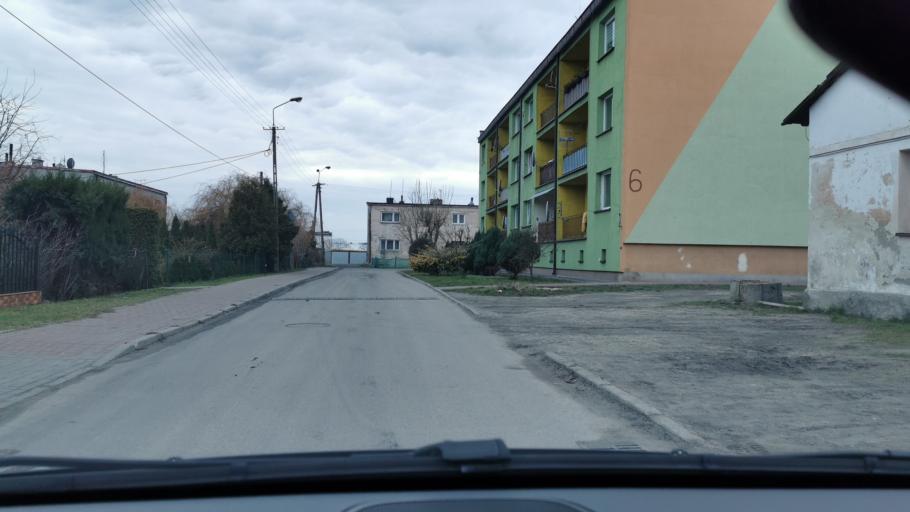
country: PL
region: Masovian Voivodeship
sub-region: Powiat zyrardowski
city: Guzow
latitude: 52.1125
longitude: 20.3312
